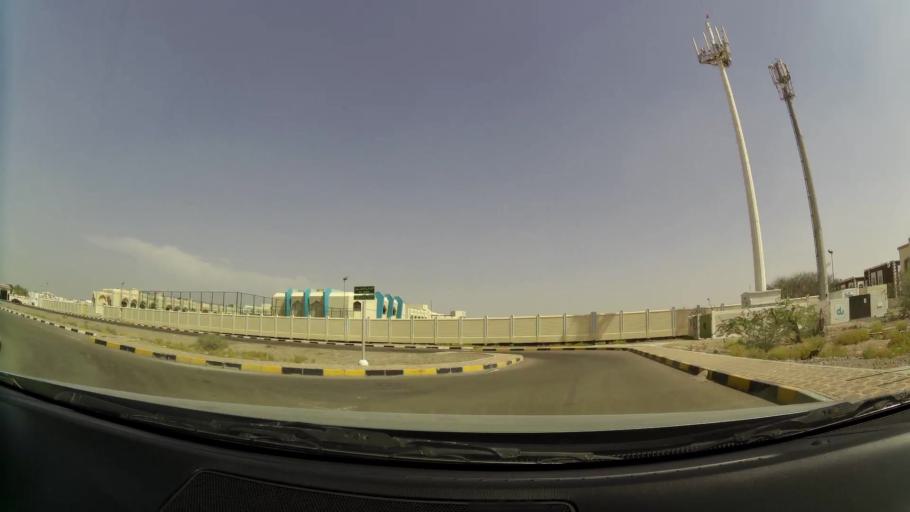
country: AE
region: Abu Dhabi
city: Al Ain
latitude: 24.2246
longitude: 55.6886
